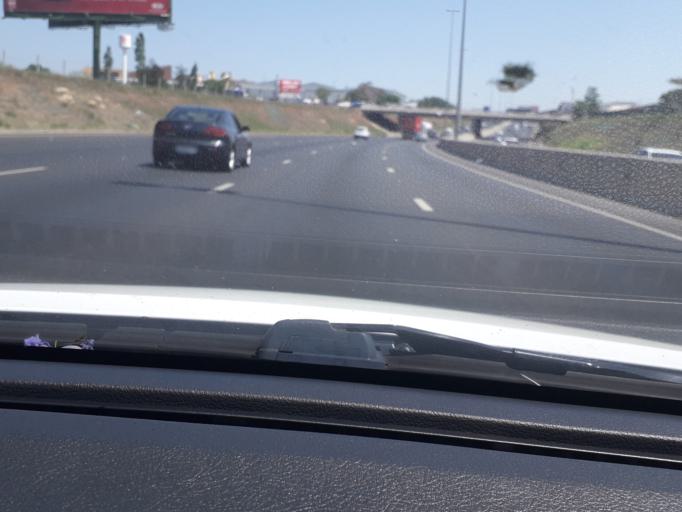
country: ZA
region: Gauteng
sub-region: Ekurhuleni Metropolitan Municipality
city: Germiston
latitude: -26.1725
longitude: 28.1934
